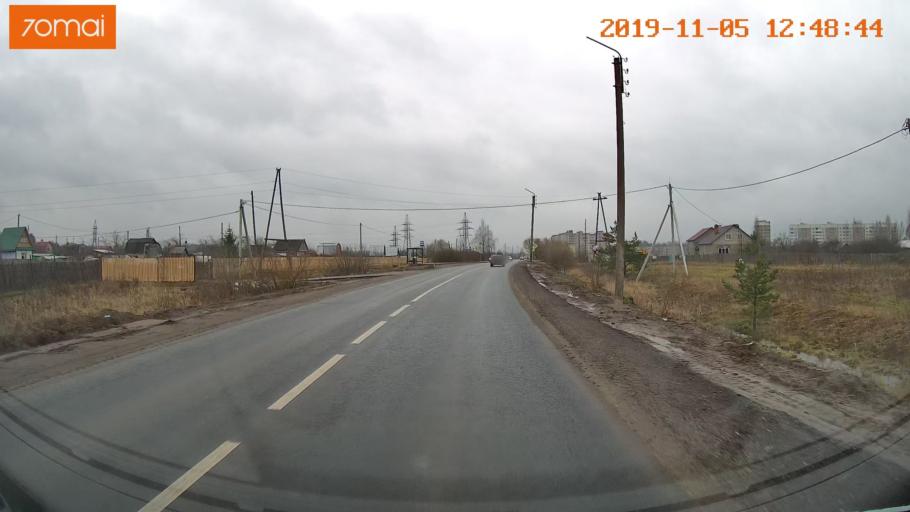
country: RU
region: Ivanovo
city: Kokhma
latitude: 56.9588
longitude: 41.1005
